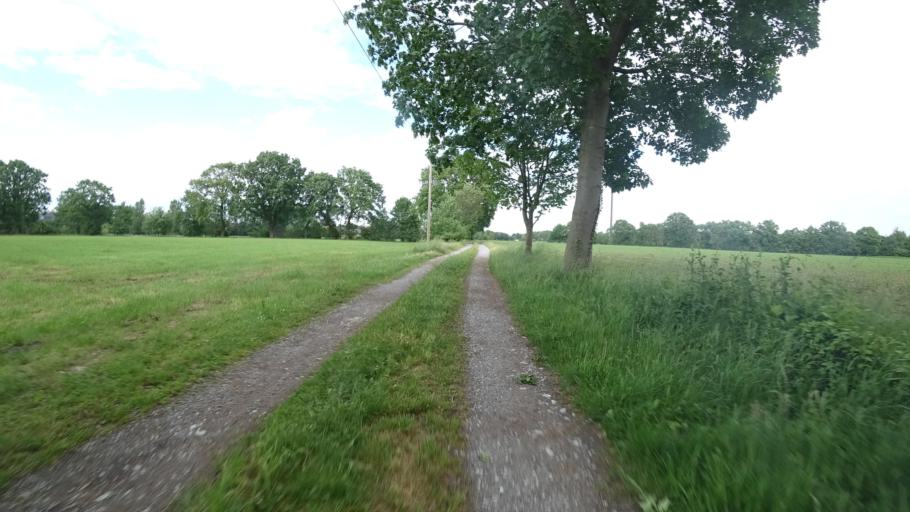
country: DE
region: North Rhine-Westphalia
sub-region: Regierungsbezirk Detmold
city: Guetersloh
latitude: 51.8800
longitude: 8.4209
